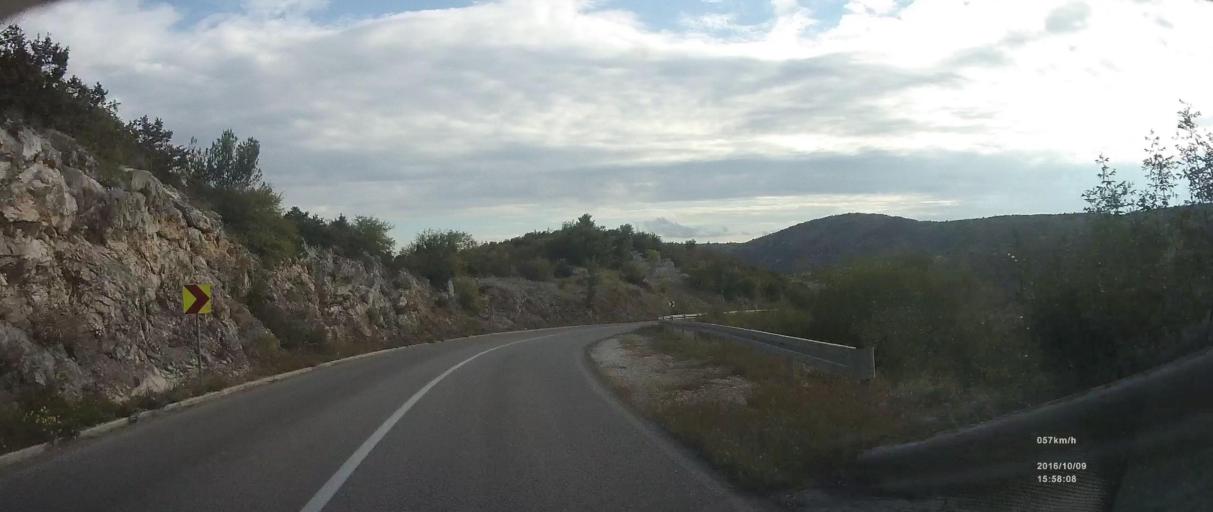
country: HR
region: Splitsko-Dalmatinska
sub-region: Grad Trogir
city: Trogir
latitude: 43.5717
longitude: 16.2433
